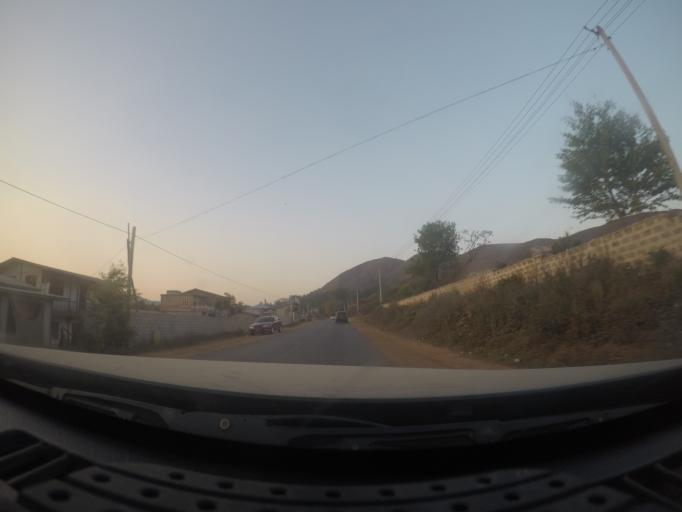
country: MM
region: Shan
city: Taunggyi
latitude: 20.7149
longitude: 97.0582
